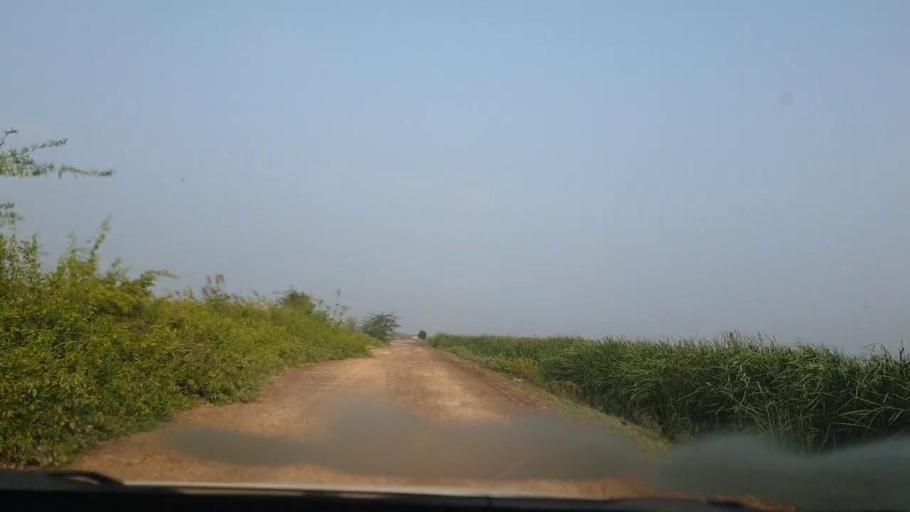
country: PK
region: Sindh
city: Tando Muhammad Khan
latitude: 25.0932
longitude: 68.4783
